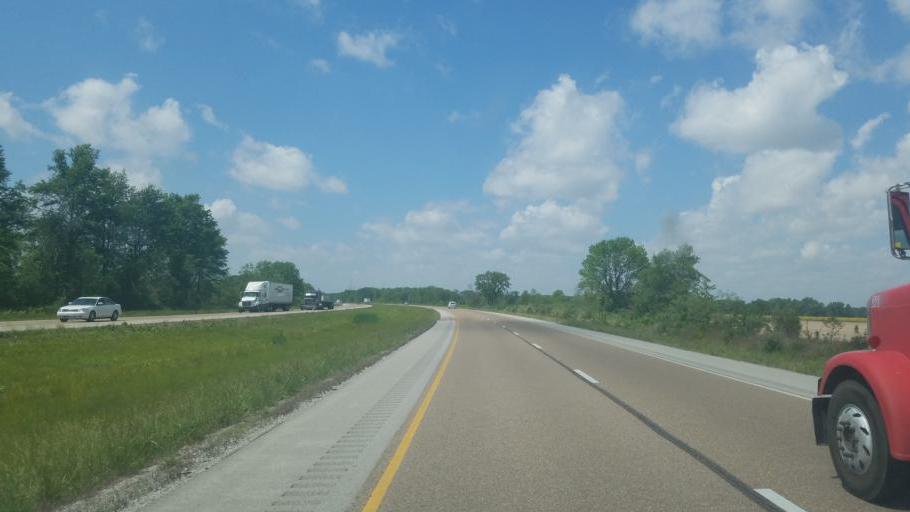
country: US
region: Illinois
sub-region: Cumberland County
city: Greenup
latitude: 39.2730
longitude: -88.1103
